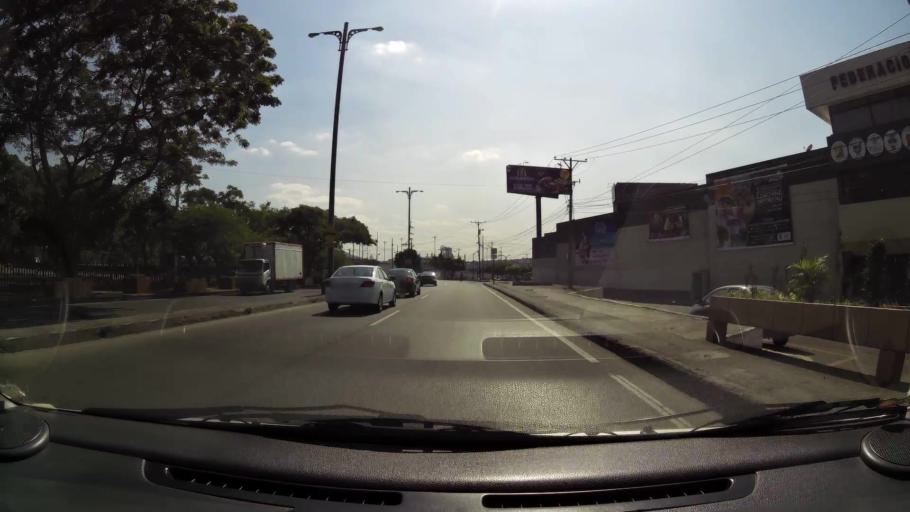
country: EC
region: Guayas
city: Guayaquil
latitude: -2.1622
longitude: -79.9253
